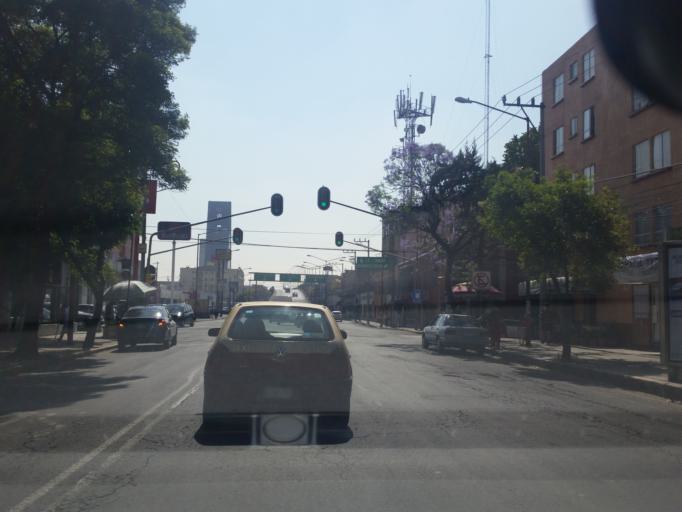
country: MX
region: Mexico City
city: Cuauhtemoc
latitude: 19.4551
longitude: -99.1592
